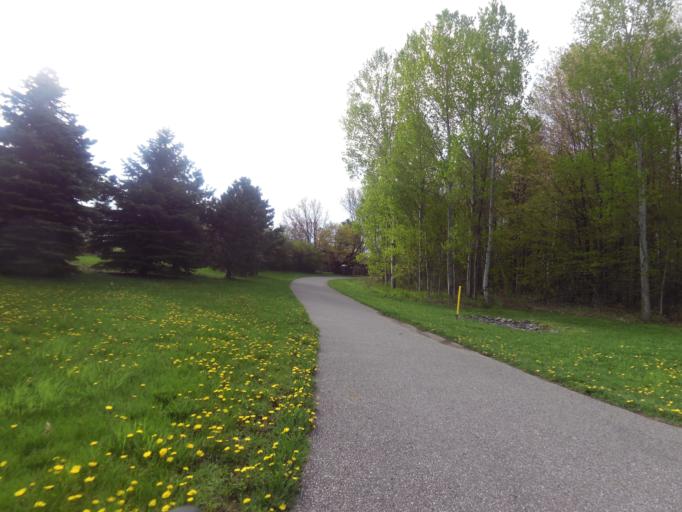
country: CA
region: Ontario
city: Bells Corners
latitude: 45.3248
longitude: -75.7680
